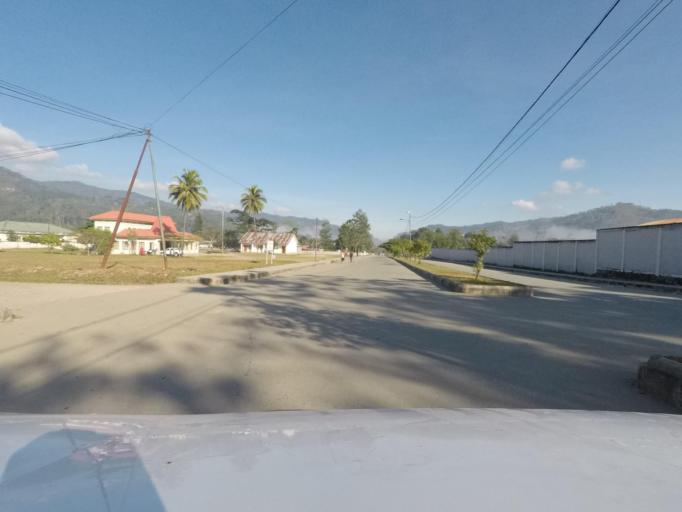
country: TL
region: Ermera
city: Gleno
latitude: -8.7237
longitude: 125.4347
